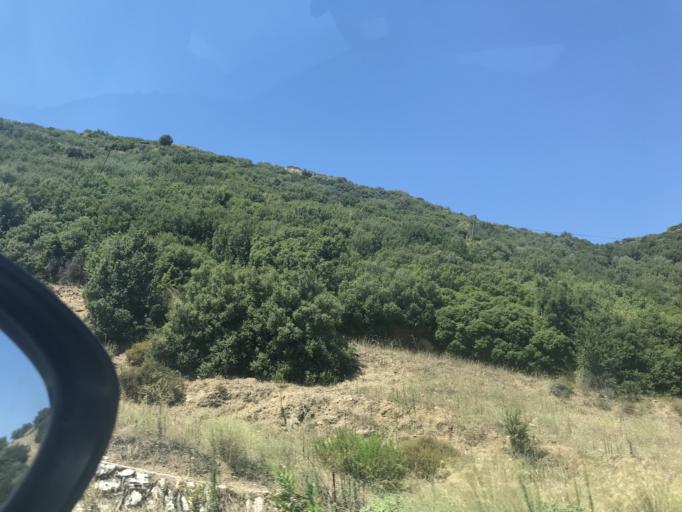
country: TR
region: Aydin
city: Akcaova
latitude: 37.5047
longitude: 28.1027
